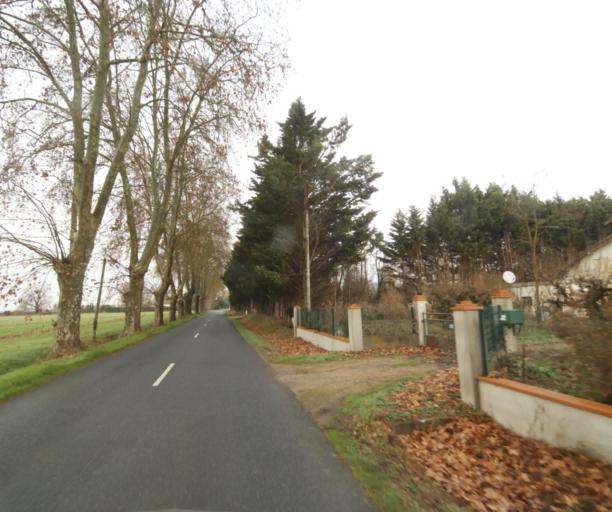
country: FR
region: Midi-Pyrenees
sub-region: Departement de la Haute-Garonne
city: Villemur-sur-Tarn
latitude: 43.8759
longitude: 1.4884
